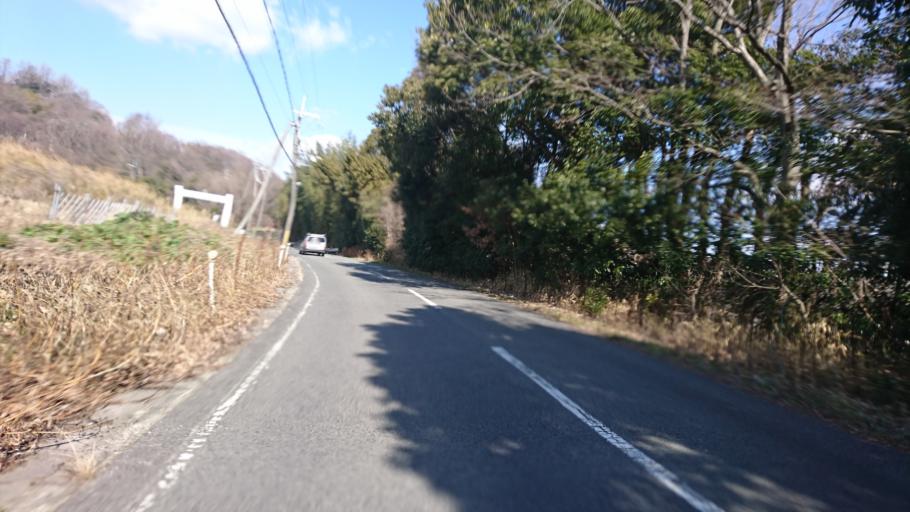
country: JP
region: Hyogo
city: Kakogawacho-honmachi
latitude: 34.8326
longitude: 134.8229
